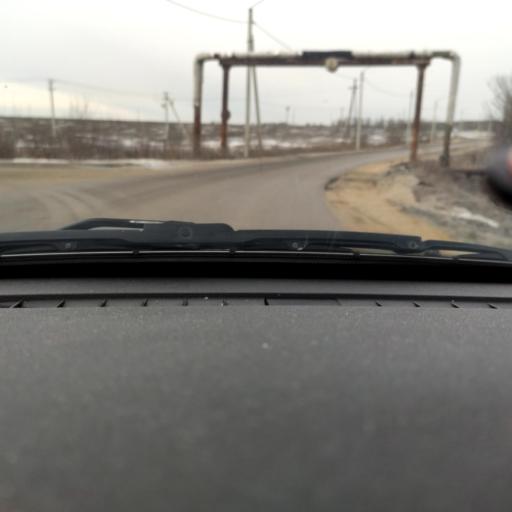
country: RU
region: Voronezj
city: Maslovka
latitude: 51.5781
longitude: 39.3130
